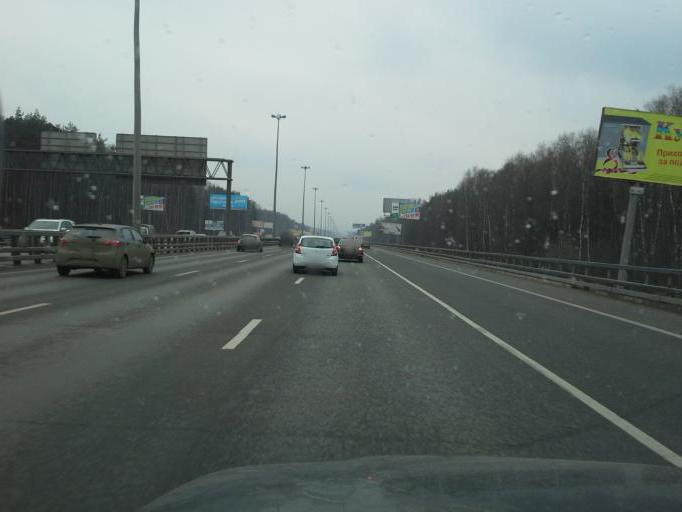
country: RU
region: Moscow
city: Solntsevo
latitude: 55.6250
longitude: 37.4140
